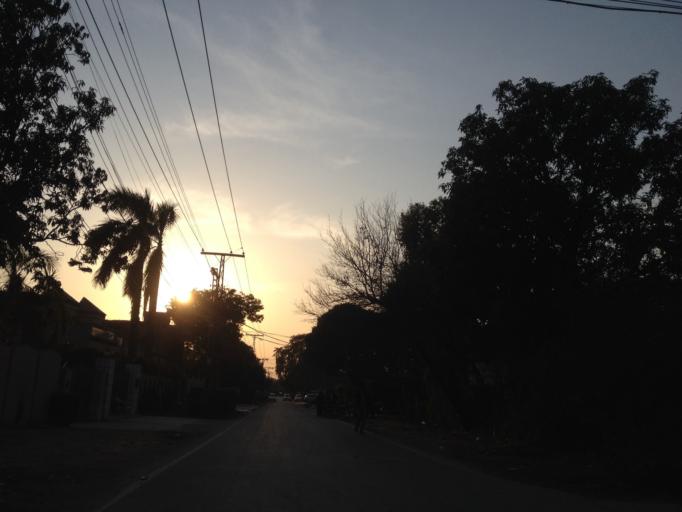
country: PK
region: Punjab
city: Lahore
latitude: 31.5006
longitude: 74.3313
